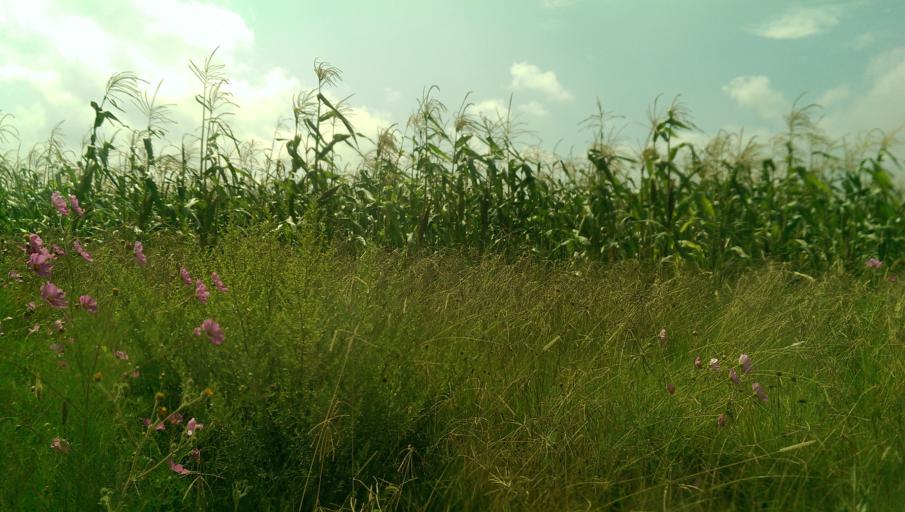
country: MX
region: Queretaro
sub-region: Huimilpan
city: San Jose Tepuzas
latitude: 20.3563
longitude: -100.3922
